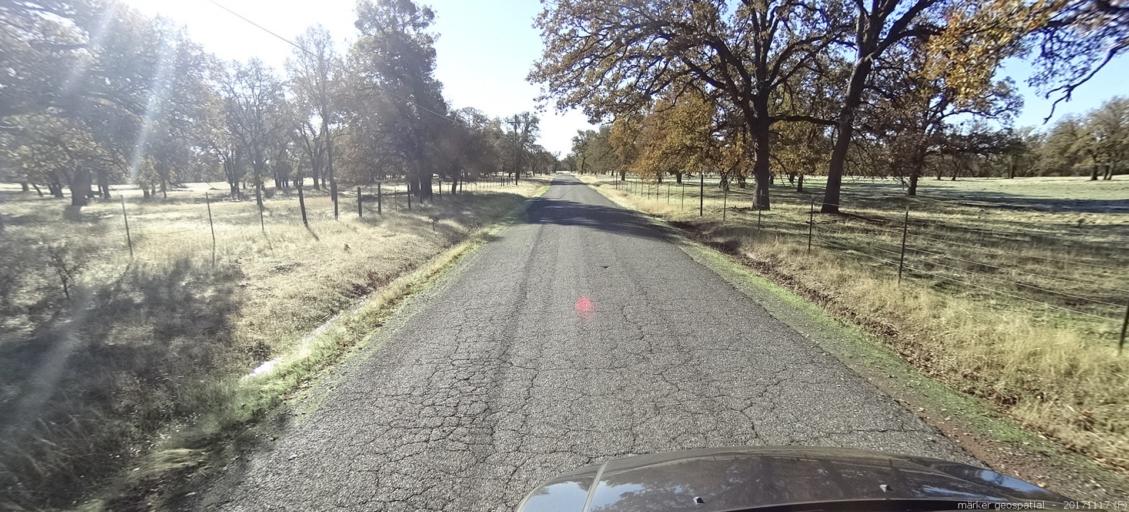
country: US
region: California
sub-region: Shasta County
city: Palo Cedro
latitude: 40.4678
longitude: -122.1910
